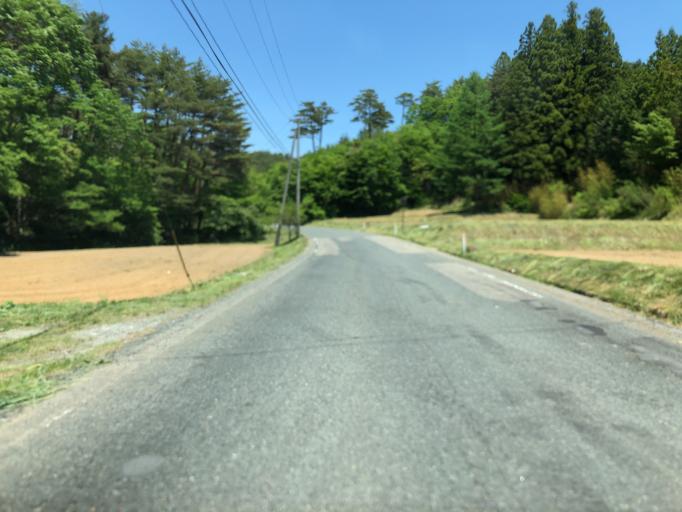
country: JP
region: Fukushima
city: Funehikimachi-funehiki
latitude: 37.5199
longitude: 140.7776
